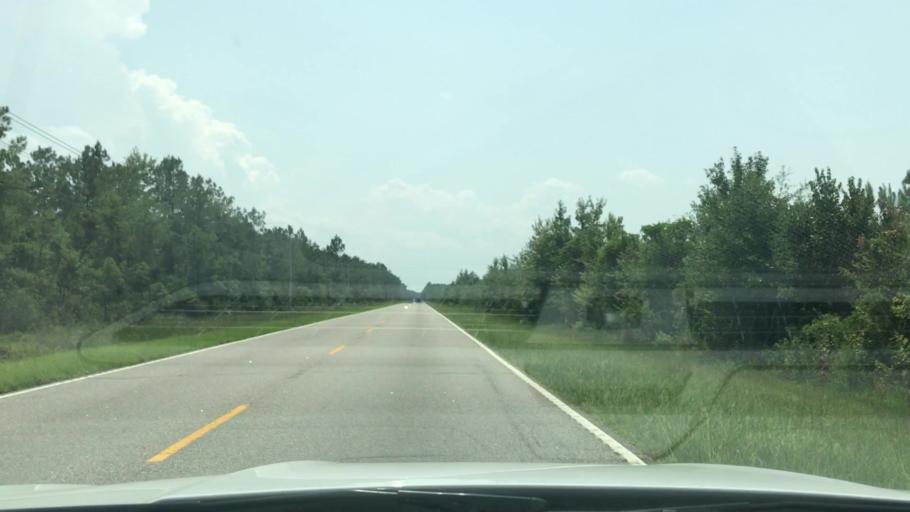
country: US
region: South Carolina
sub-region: Georgetown County
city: Georgetown
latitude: 33.5176
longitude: -79.2477
